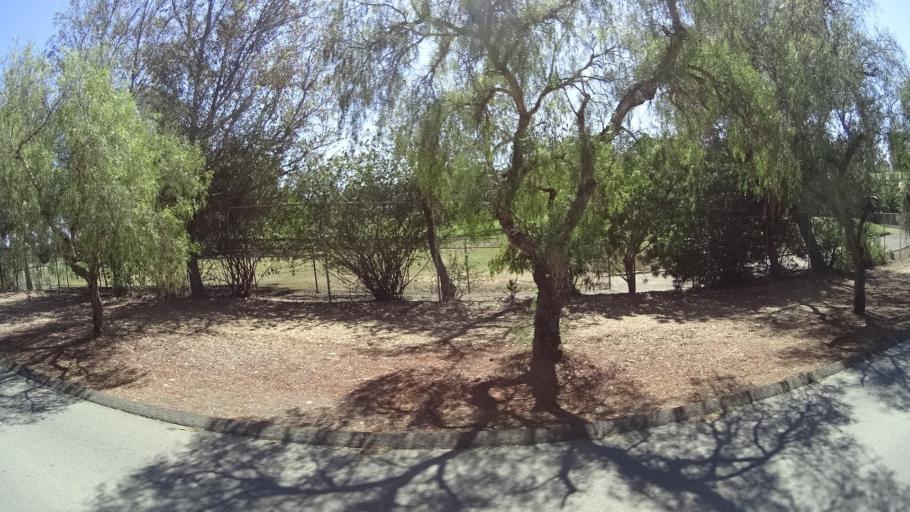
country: US
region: California
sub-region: San Diego County
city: Rancho Santa Fe
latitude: 33.0250
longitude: -117.2129
